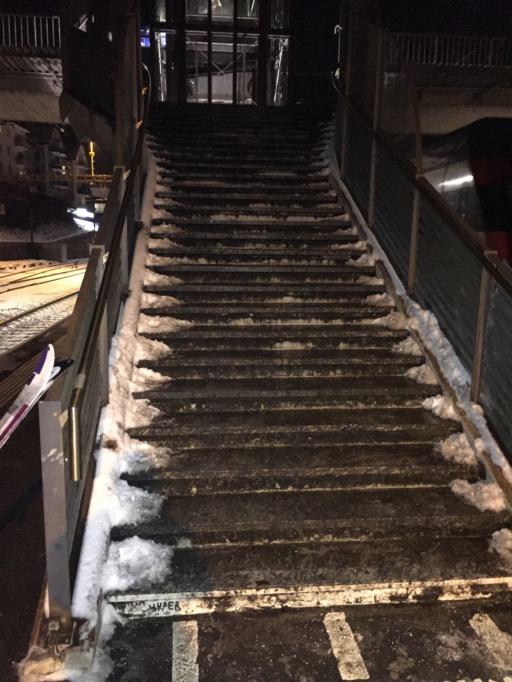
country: CH
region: Zurich
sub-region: Bezirk Horgen
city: Thalwil
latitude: 47.2953
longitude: 8.5650
